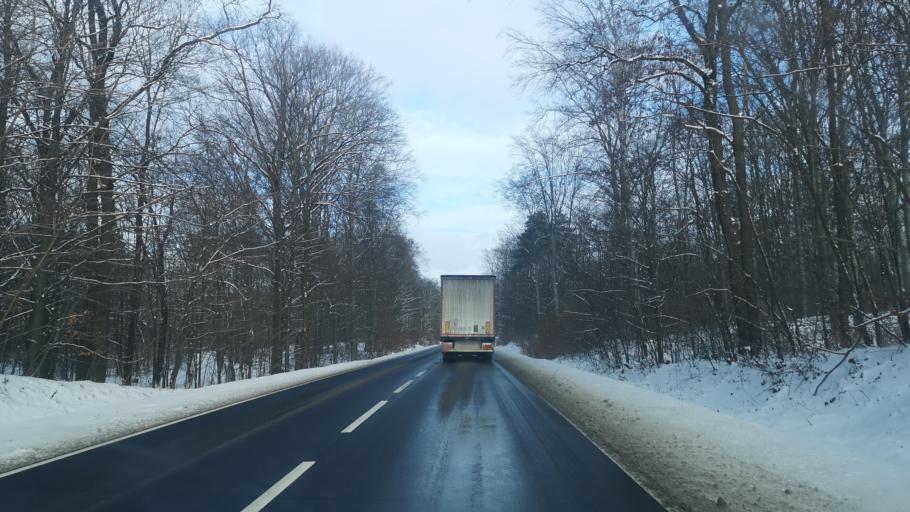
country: PL
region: Subcarpathian Voivodeship
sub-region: Powiat przeworski
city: Sieniawa
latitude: 50.2067
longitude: 22.6388
